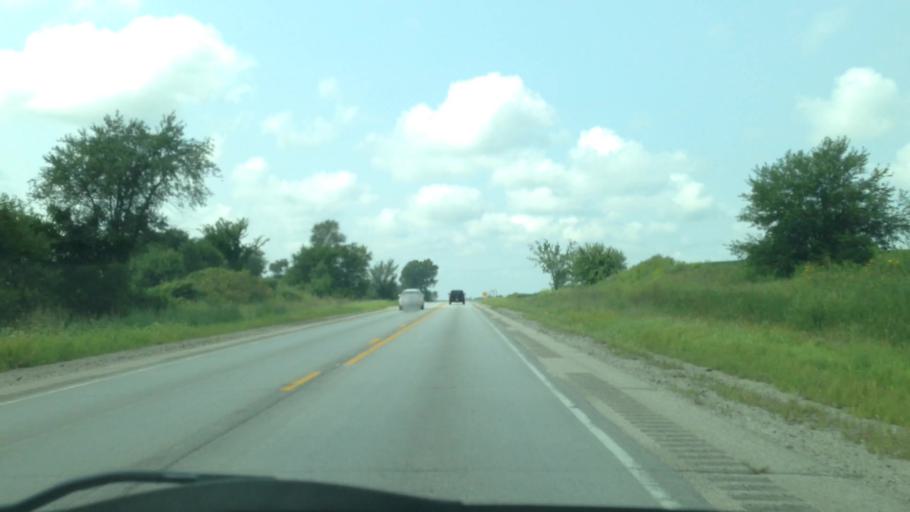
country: US
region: Iowa
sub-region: Benton County
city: Walford
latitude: 41.8898
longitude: -91.8181
